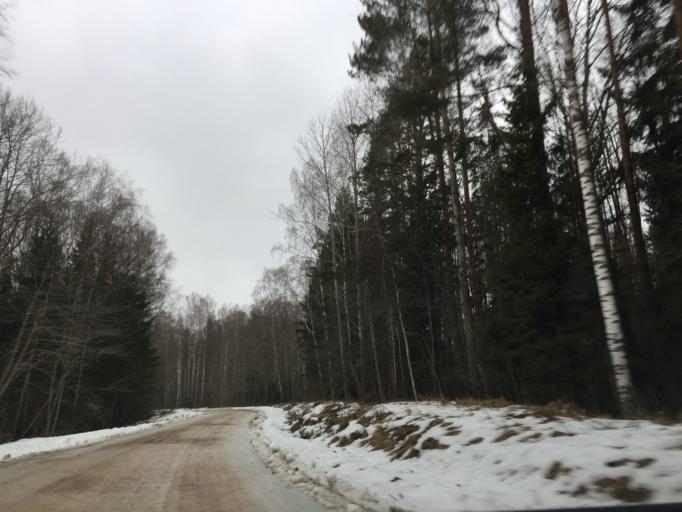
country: LV
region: Salacgrivas
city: Salacgriva
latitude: 57.6486
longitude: 24.4227
